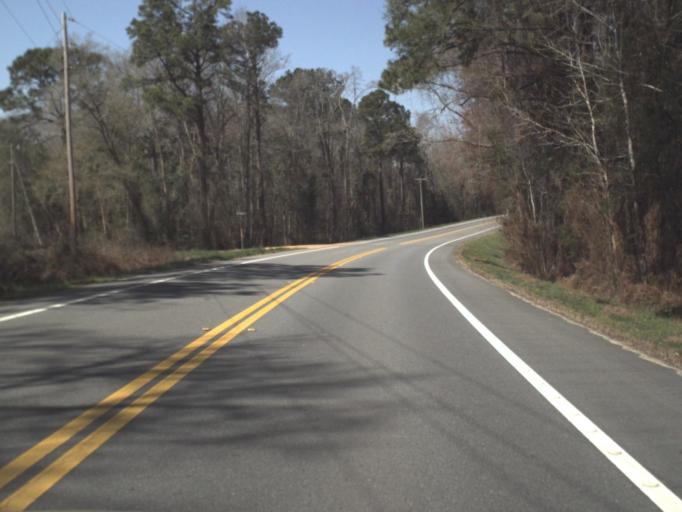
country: US
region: Florida
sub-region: Jackson County
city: Sneads
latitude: 30.6338
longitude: -85.0350
